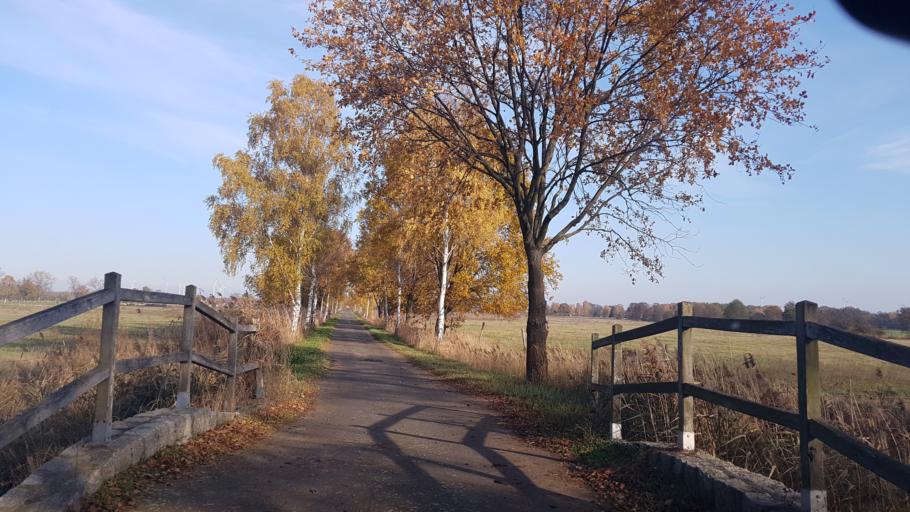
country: DE
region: Brandenburg
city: Falkenberg
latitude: 51.6222
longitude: 13.3067
